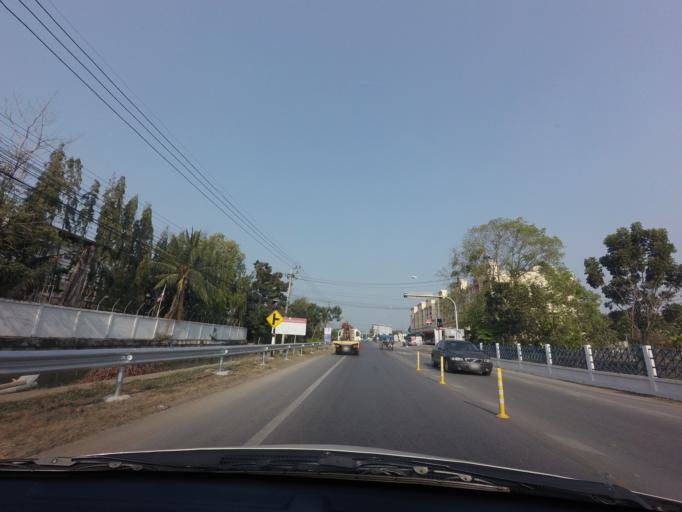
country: TH
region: Bangkok
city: Thawi Watthana
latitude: 13.8115
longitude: 100.3486
